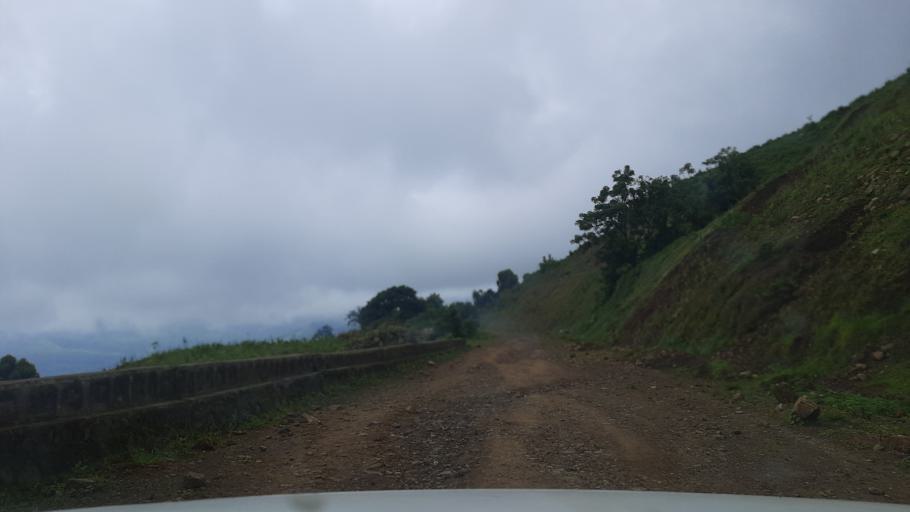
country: ET
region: Southern Nations, Nationalities, and People's Region
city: Bonga
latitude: 7.1137
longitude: 36.5410
